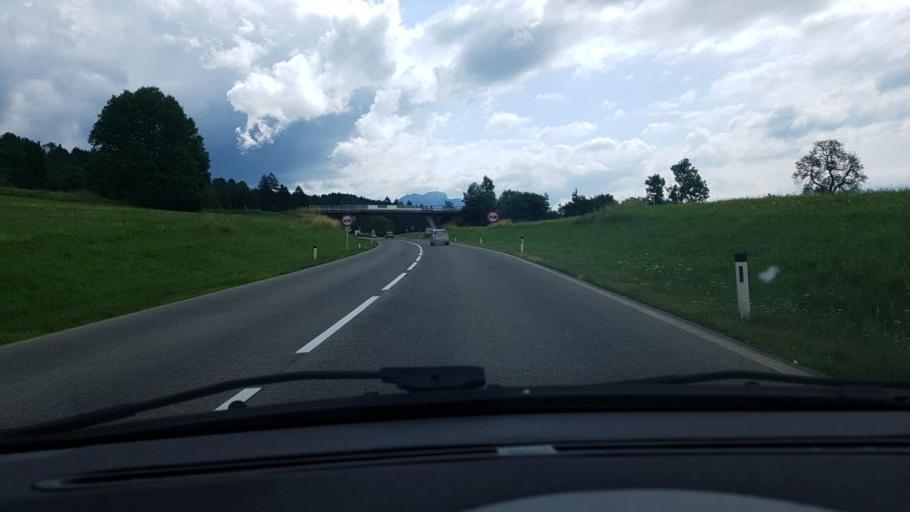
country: AT
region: Carinthia
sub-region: Politischer Bezirk Villach Land
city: Stockenboi
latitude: 46.6226
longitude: 13.4915
